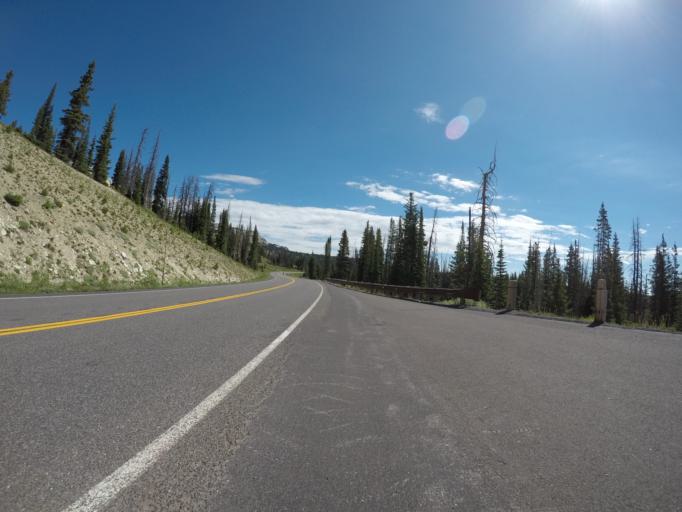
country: US
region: Wyoming
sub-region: Carbon County
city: Saratoga
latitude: 41.3175
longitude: -106.3463
